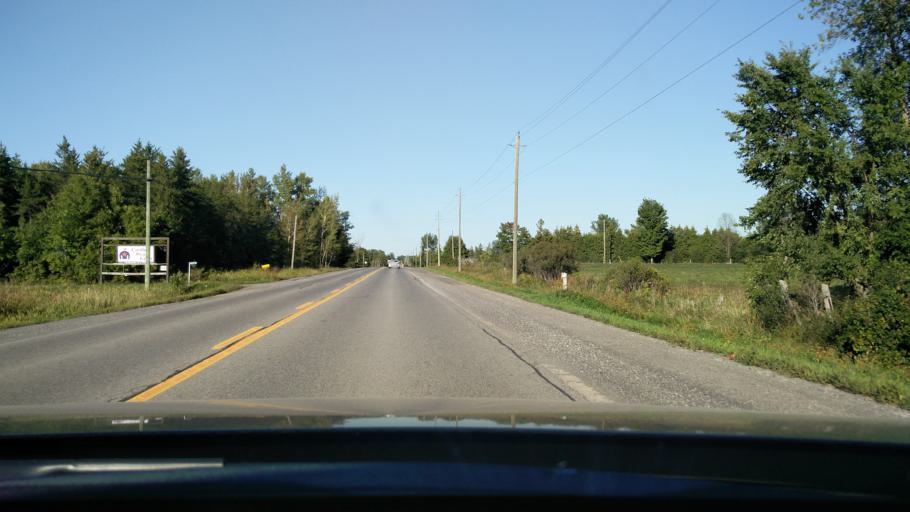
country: CA
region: Ontario
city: Carleton Place
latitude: 45.1159
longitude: -75.9639
